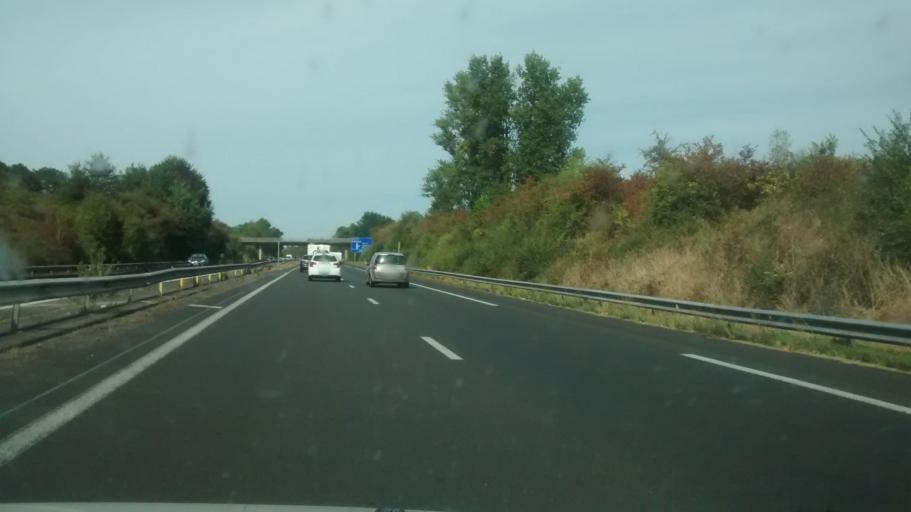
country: FR
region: Aquitaine
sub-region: Departement de la Gironde
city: Castets-en-Dorthe
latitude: 44.5306
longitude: -0.1618
